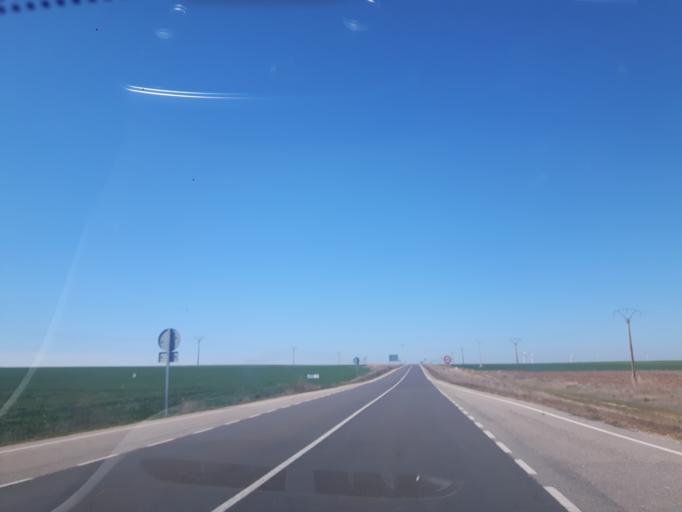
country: ES
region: Castille and Leon
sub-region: Provincia de Salamanca
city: Coca de Alba
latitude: 40.8713
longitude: -5.3787
